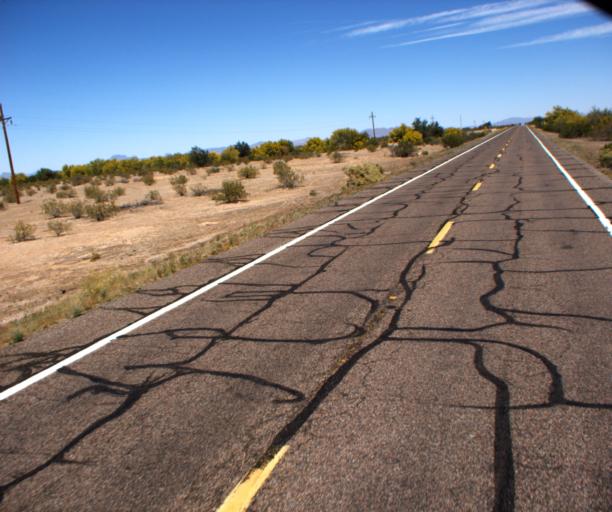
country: US
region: Arizona
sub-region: Maricopa County
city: Gila Bend
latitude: 32.8057
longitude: -112.7964
